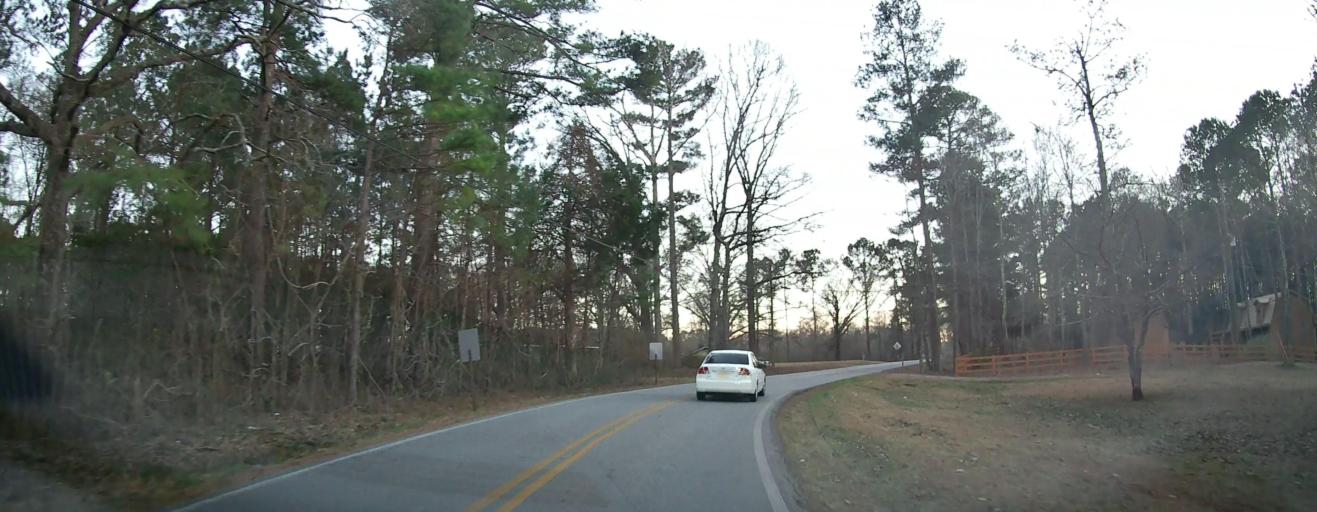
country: US
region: Georgia
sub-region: Troup County
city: La Grange
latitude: 33.0613
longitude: -84.9680
